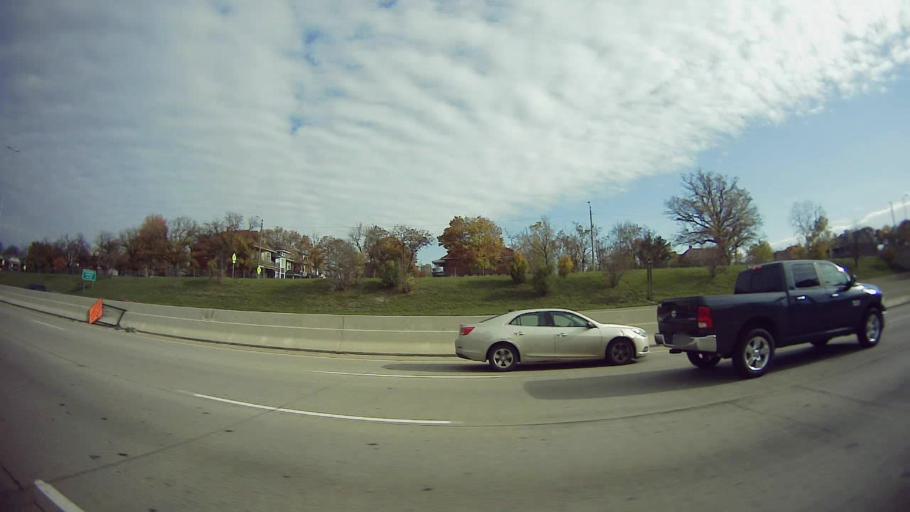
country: US
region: Michigan
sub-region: Wayne County
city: Highland Park
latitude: 42.3746
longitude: -83.0871
